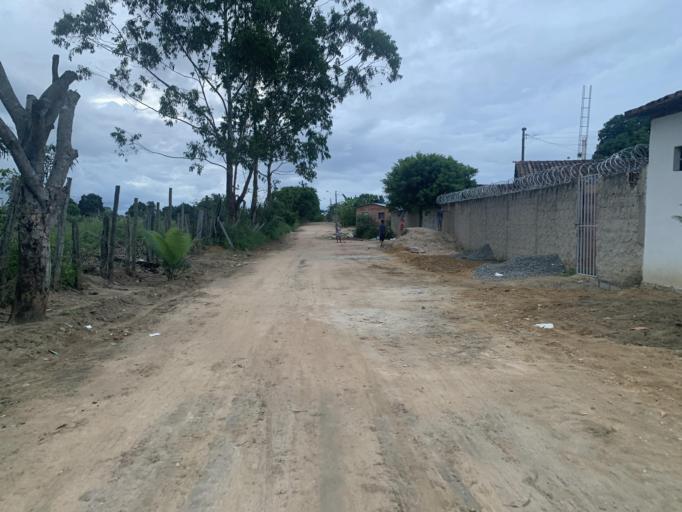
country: BR
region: Bahia
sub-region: Medeiros Neto
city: Medeiros Neto
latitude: -17.3932
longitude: -40.2300
